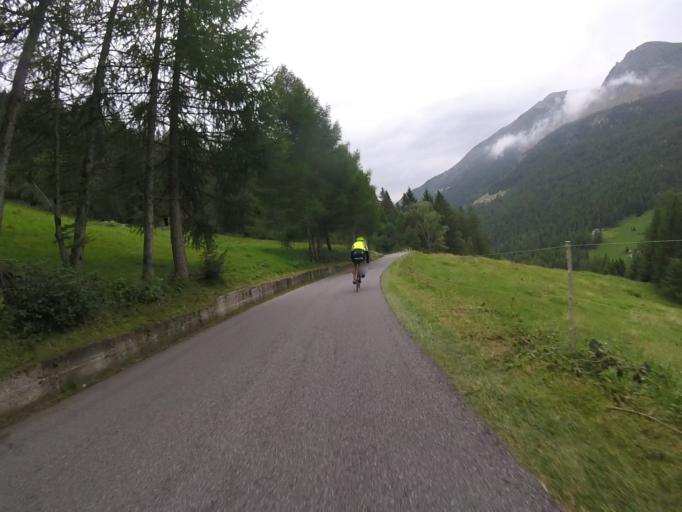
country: IT
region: Lombardy
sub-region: Provincia di Brescia
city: Monno
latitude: 46.2355
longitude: 10.3210
